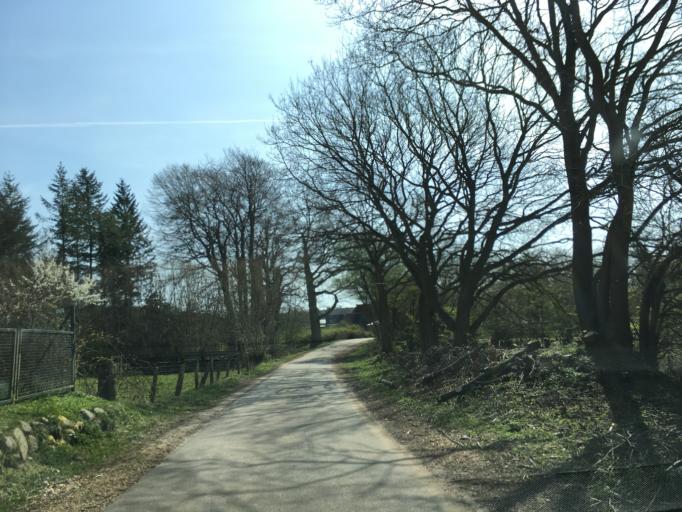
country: DE
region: Schleswig-Holstein
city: Felm
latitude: 54.4144
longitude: 10.0775
